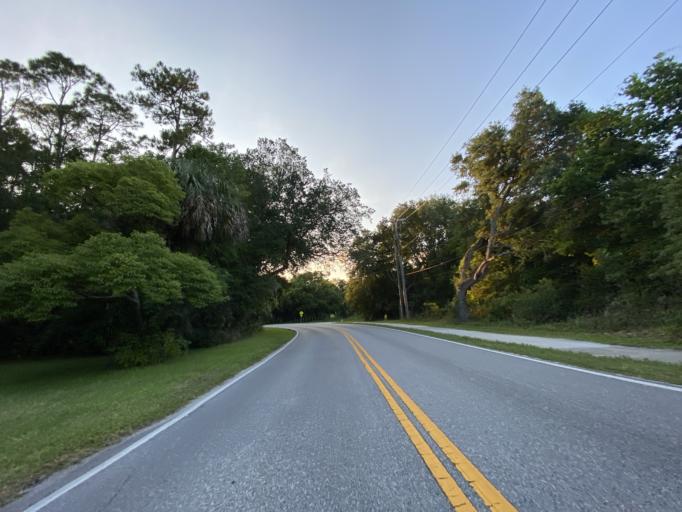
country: US
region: Florida
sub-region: Volusia County
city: Port Orange
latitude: 29.1481
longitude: -81.0035
